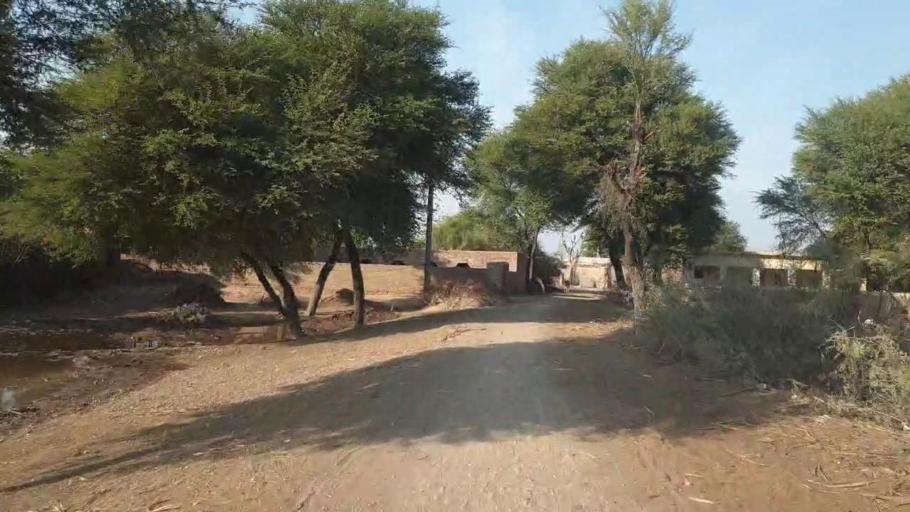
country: PK
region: Sindh
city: Chambar
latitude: 25.3189
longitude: 68.7902
